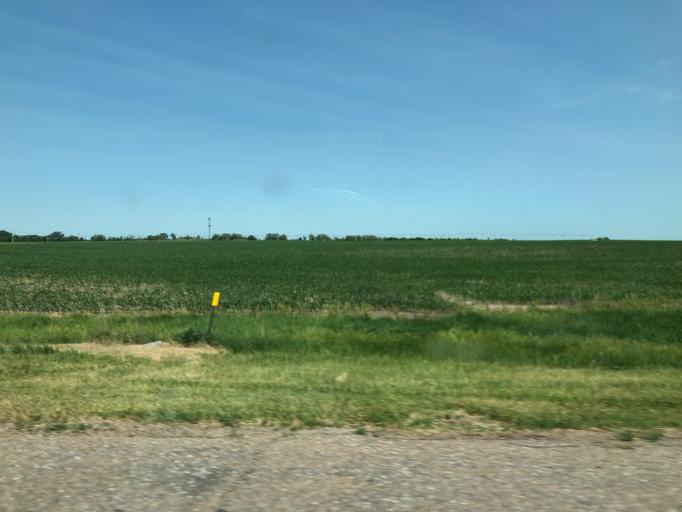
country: US
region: Nebraska
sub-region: Thayer County
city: Hebron
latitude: 40.2752
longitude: -97.5765
